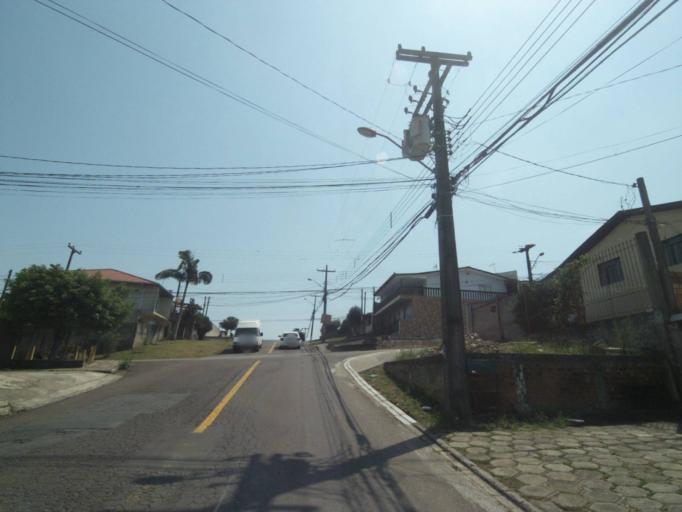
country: BR
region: Parana
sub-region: Sao Jose Dos Pinhais
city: Sao Jose dos Pinhais
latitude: -25.5209
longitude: -49.2658
